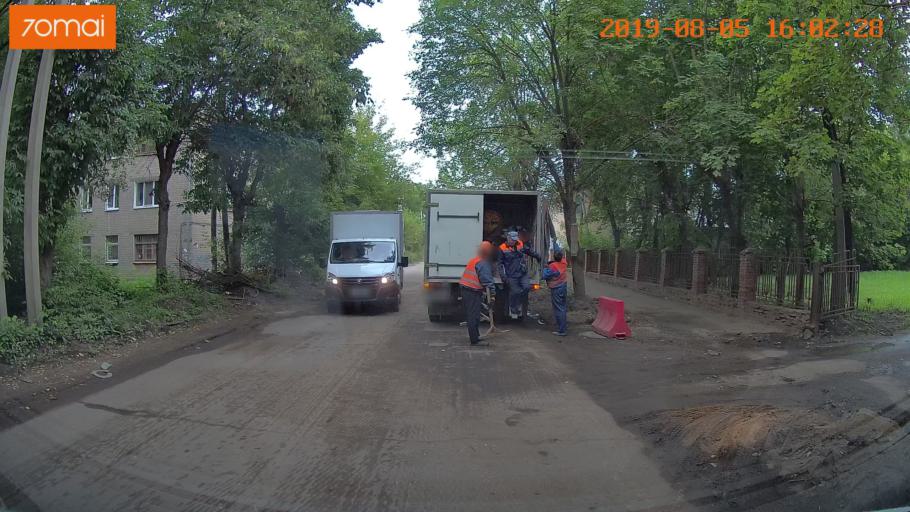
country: RU
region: Ivanovo
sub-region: Gorod Ivanovo
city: Ivanovo
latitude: 56.9770
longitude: 40.9631
